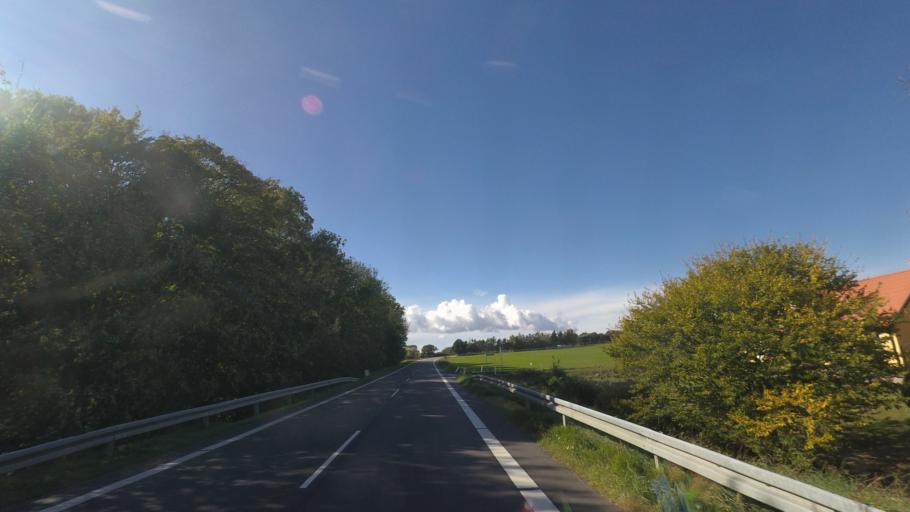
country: DK
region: Capital Region
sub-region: Bornholm Kommune
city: Akirkeby
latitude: 55.0691
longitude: 14.9778
